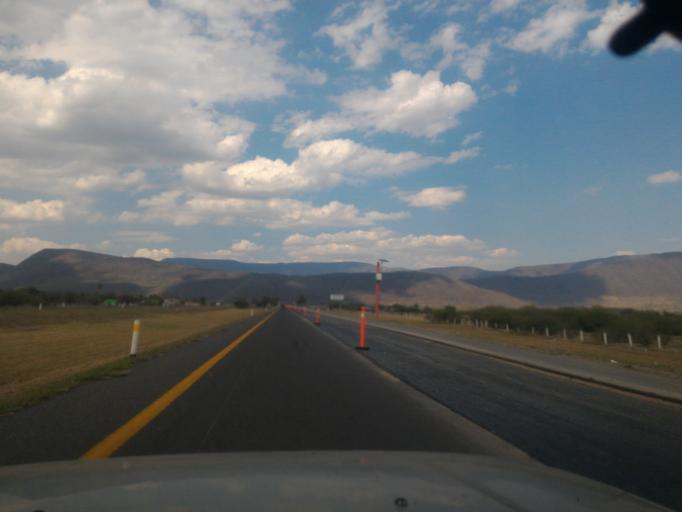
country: MX
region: Jalisco
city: Zacoalco de Torres
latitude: 20.1536
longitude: -103.5022
